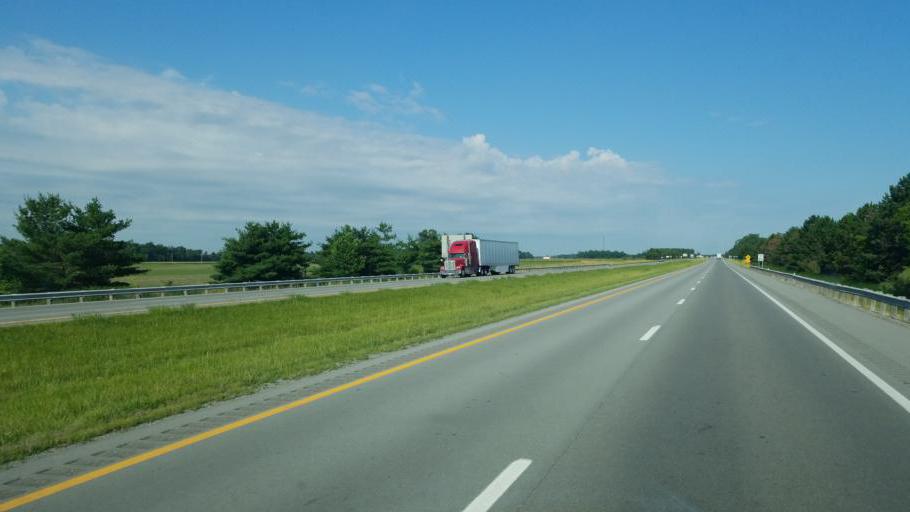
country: US
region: Ohio
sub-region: Hancock County
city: Findlay
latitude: 40.9859
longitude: -83.5872
